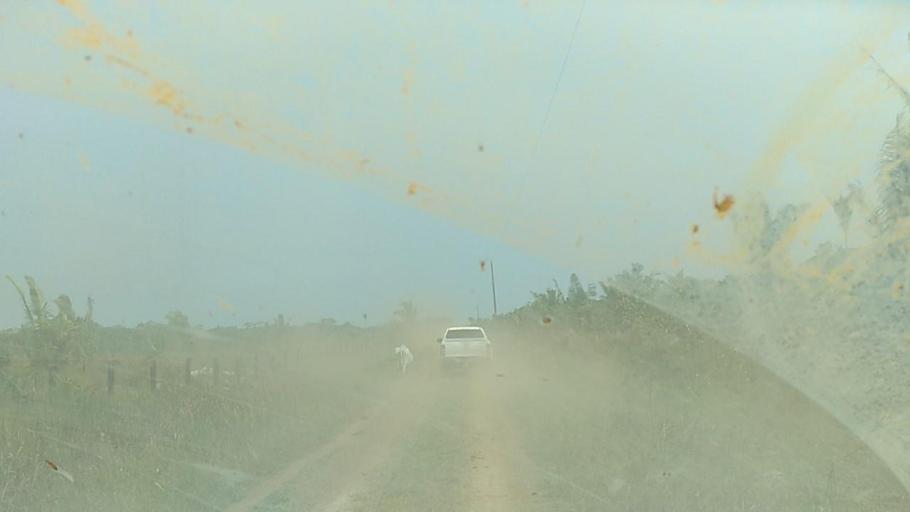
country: BR
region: Rondonia
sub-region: Porto Velho
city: Porto Velho
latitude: -8.9735
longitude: -64.3863
